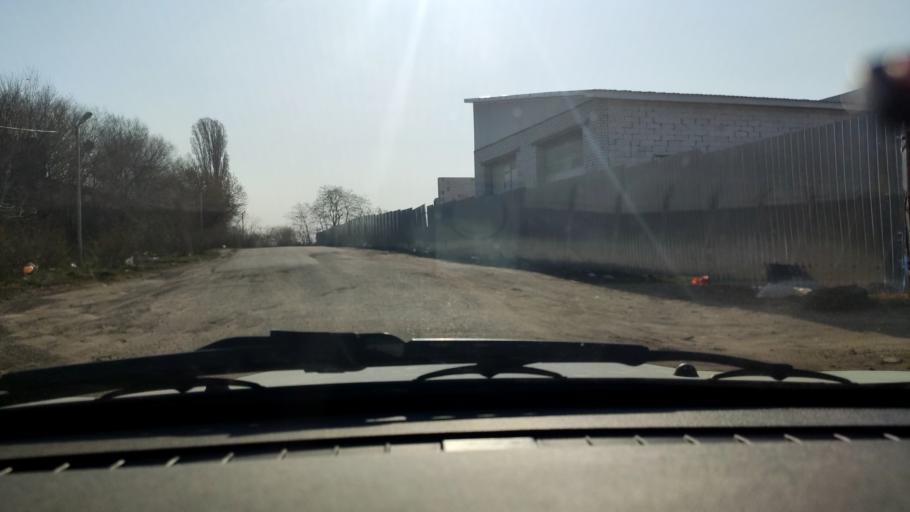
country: RU
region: Voronezj
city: Voronezh
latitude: 51.6402
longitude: 39.1244
